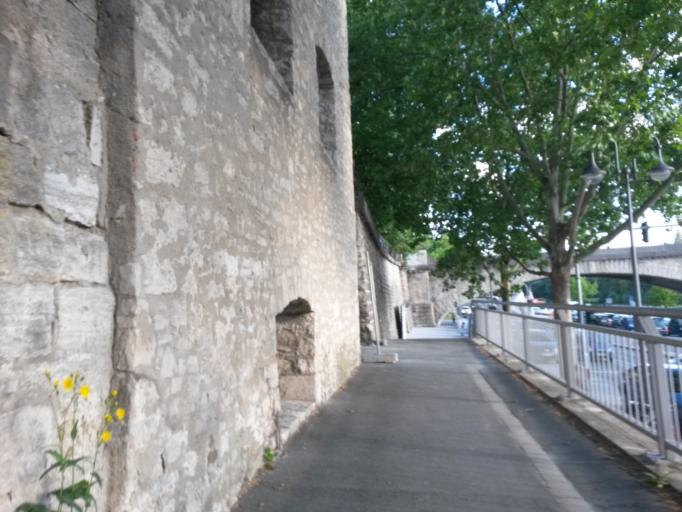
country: DE
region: Bavaria
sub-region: Regierungsbezirk Unterfranken
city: Wuerzburg
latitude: 49.7871
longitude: 9.9280
